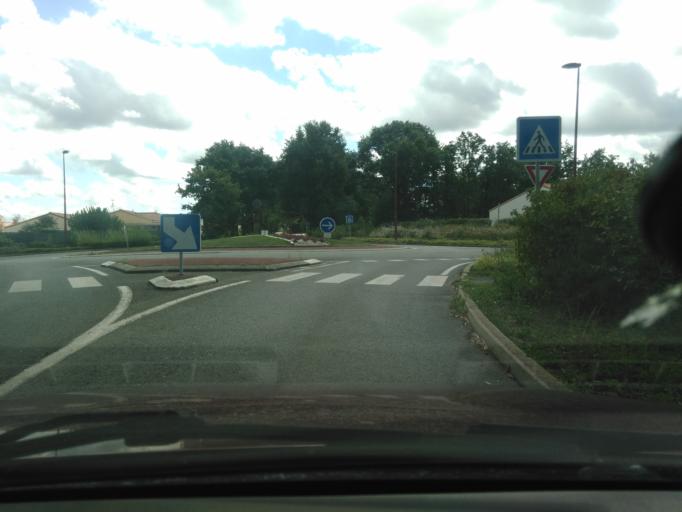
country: FR
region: Pays de la Loire
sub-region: Departement de la Vendee
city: La Ferriere
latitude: 46.7222
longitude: -1.3163
